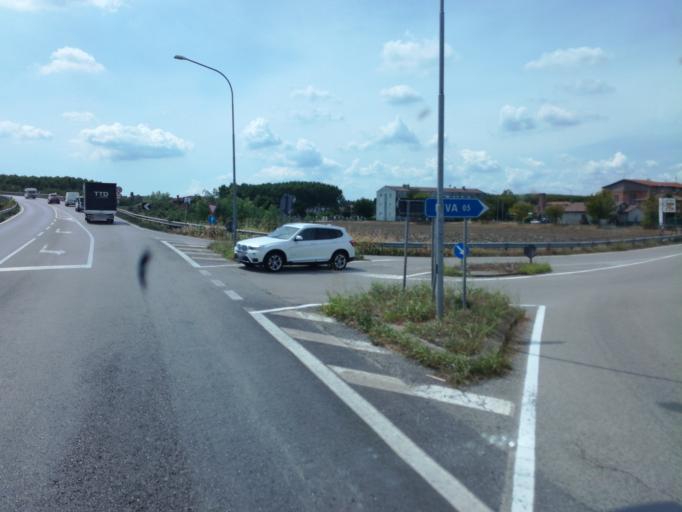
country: IT
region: Emilia-Romagna
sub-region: Provincia di Ferrara
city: Mesola
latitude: 44.9321
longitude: 12.2285
